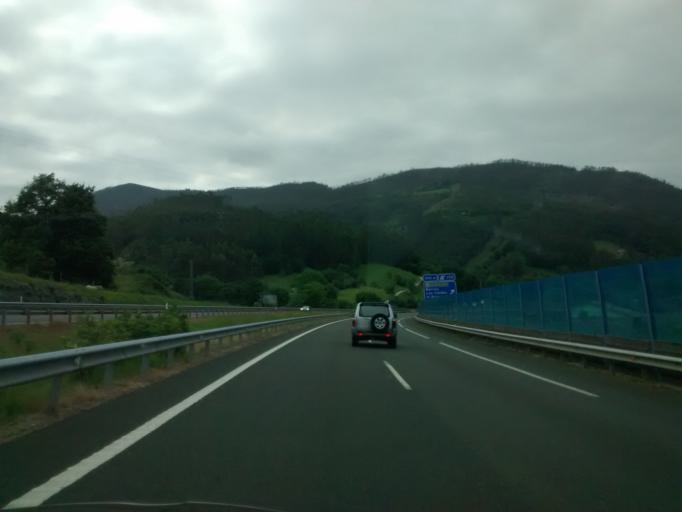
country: ES
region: Cantabria
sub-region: Provincia de Cantabria
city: Los Corrales de Buelna
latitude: 43.2770
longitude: -4.0798
